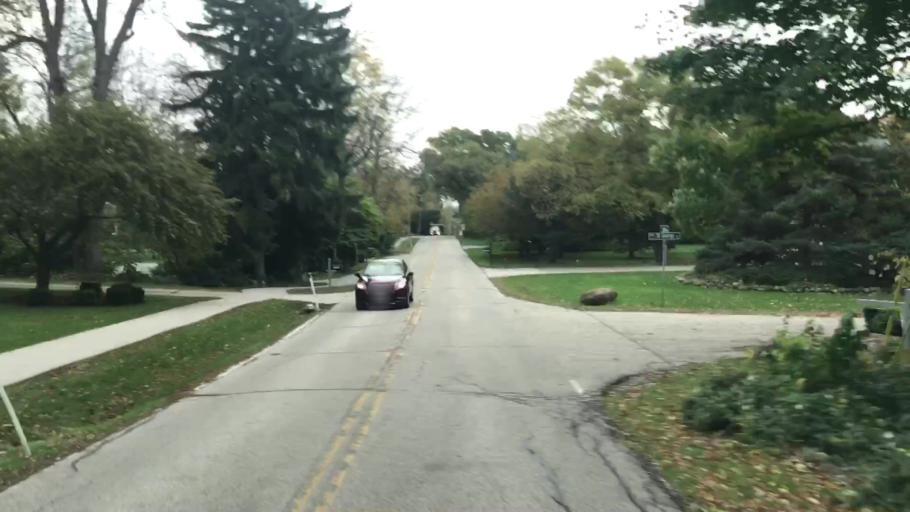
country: US
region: Wisconsin
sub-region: Waukesha County
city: Elm Grove
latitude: 43.0459
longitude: -88.0894
